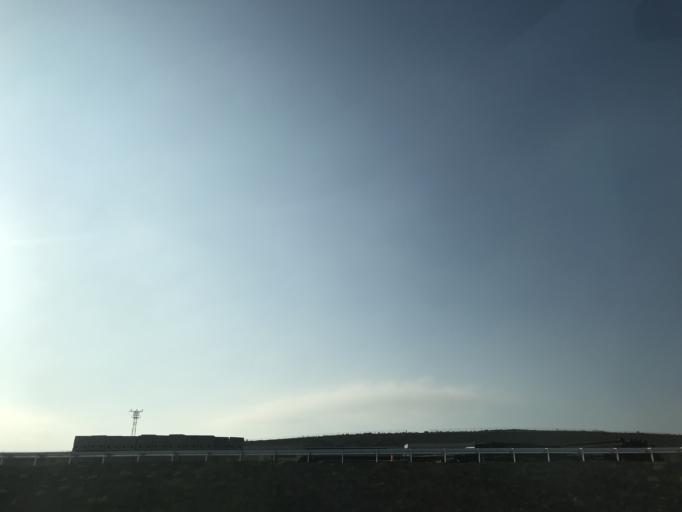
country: TR
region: Balikesir
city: Gobel
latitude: 40.0416
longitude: 28.2208
